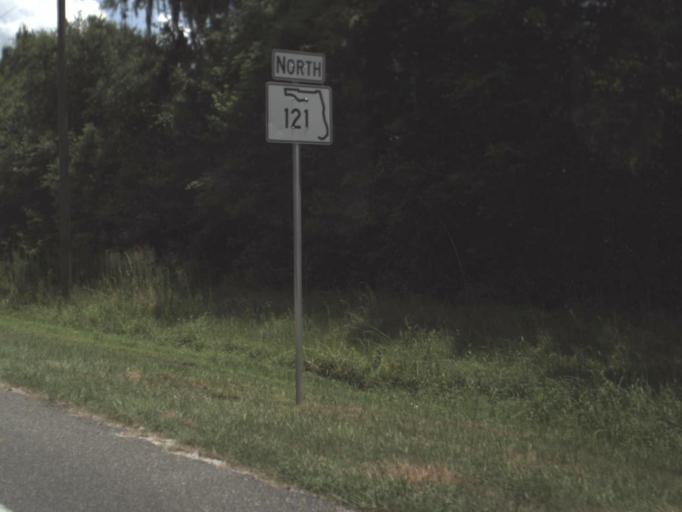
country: US
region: Florida
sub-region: Alachua County
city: Alachua
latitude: 29.8010
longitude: -82.3848
